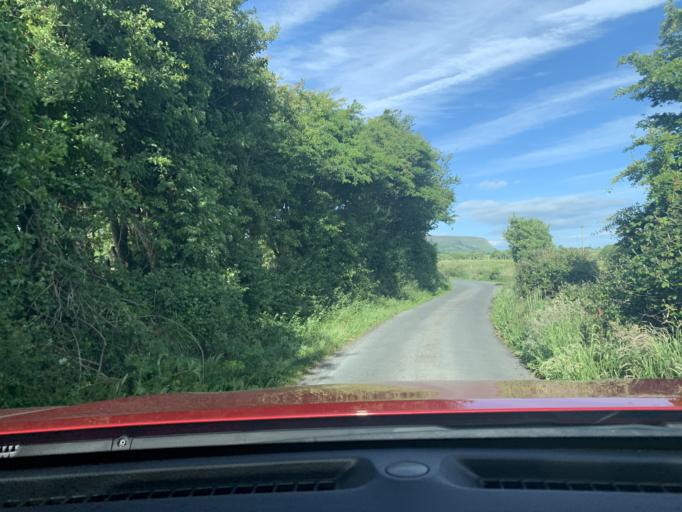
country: IE
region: Connaught
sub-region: Sligo
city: Sligo
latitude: 54.2550
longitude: -8.5091
